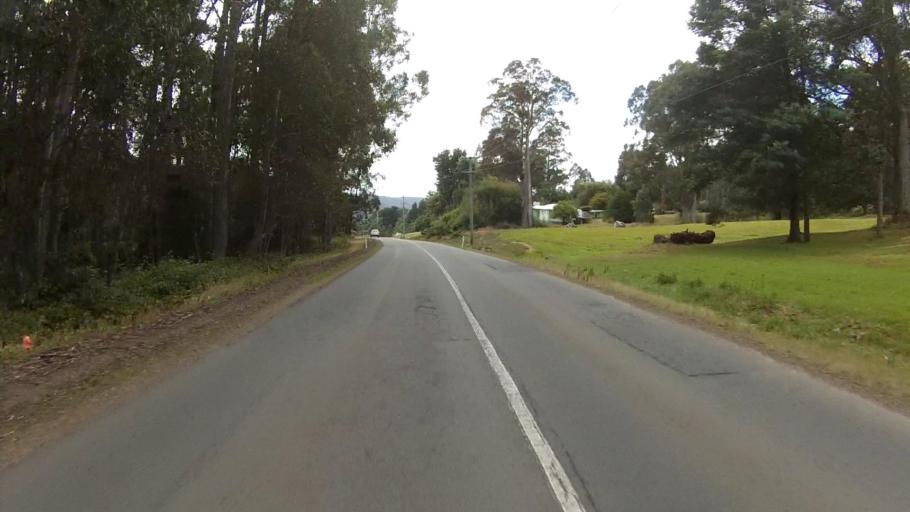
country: AU
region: Tasmania
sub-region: Kingborough
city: Kettering
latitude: -43.1163
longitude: 147.1896
